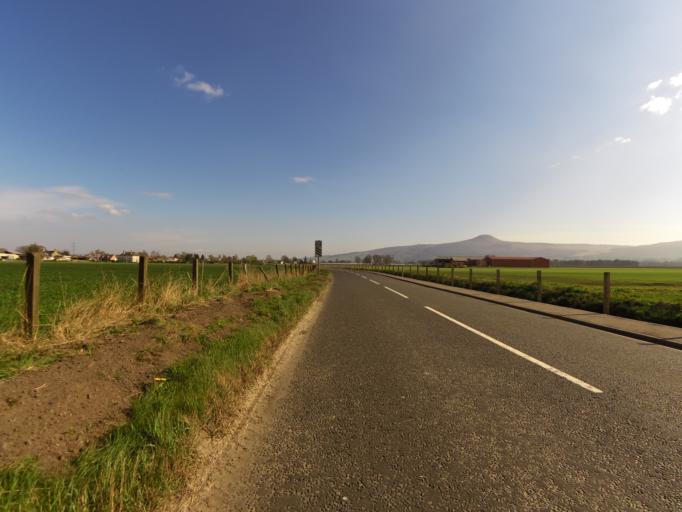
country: GB
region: Scotland
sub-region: Fife
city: Auchtermuchty
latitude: 56.2835
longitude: -3.2205
